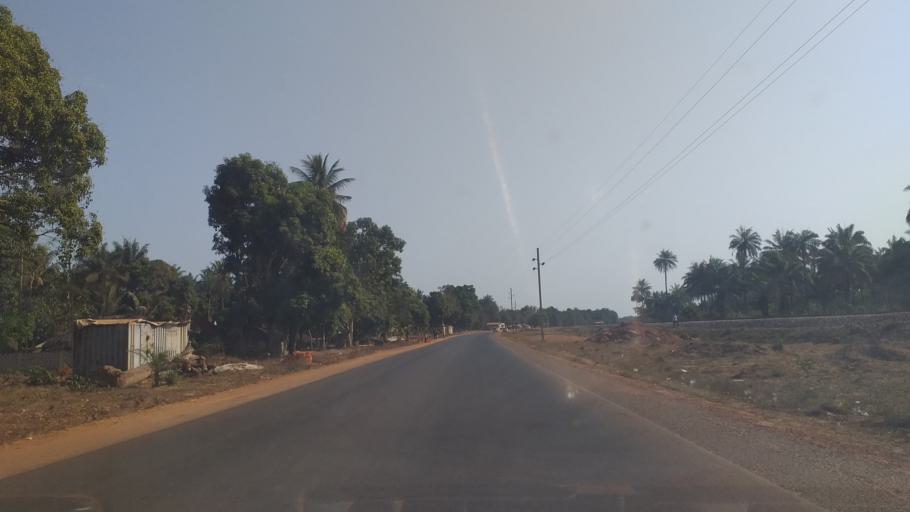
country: GN
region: Boke
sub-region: Boke Prefecture
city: Kamsar
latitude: 10.7353
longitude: -14.5160
